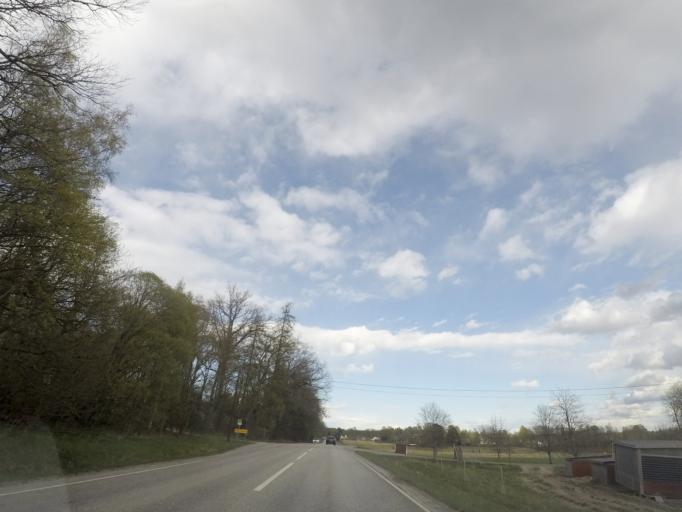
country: SE
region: Soedermanland
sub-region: Eskilstuna Kommun
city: Hallbybrunn
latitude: 59.3233
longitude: 16.4067
